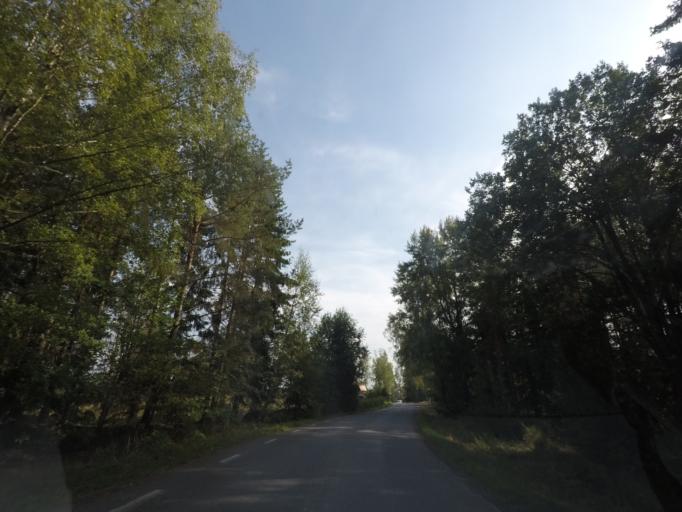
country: SE
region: Vaestmanland
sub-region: Kungsors Kommun
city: Kungsoer
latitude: 59.5088
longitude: 16.1554
